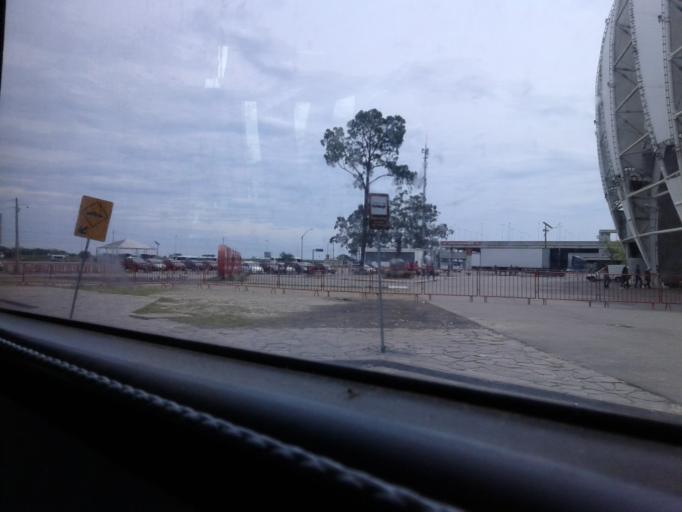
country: BR
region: Rio Grande do Sul
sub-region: Porto Alegre
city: Porto Alegre
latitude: -30.0668
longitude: -51.2357
